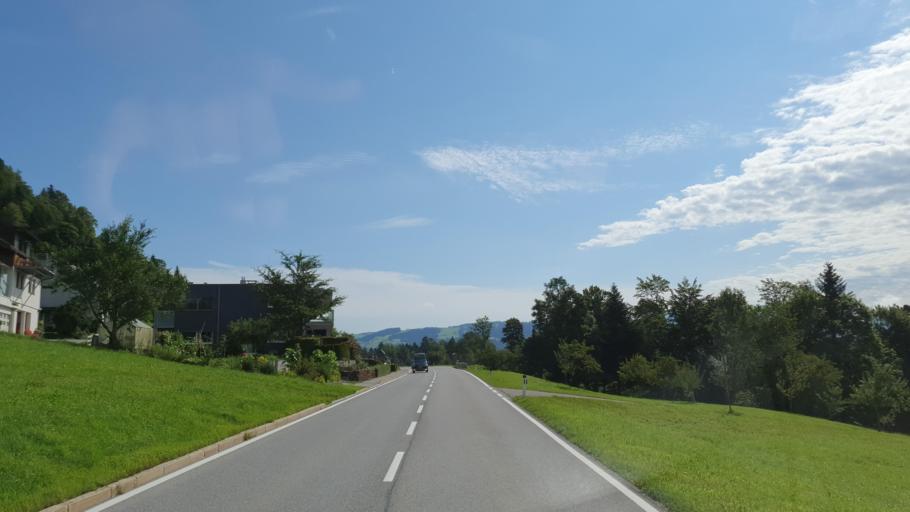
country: AT
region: Vorarlberg
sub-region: Politischer Bezirk Bregenz
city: Kennelbach
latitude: 47.4983
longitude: 9.8015
